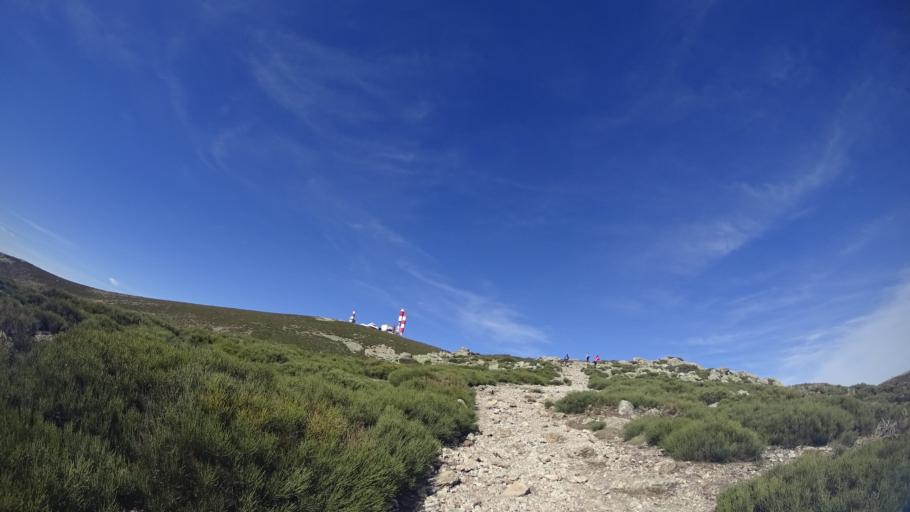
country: ES
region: Madrid
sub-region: Provincia de Madrid
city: Becerril de la Sierra
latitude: 40.7801
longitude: -3.9744
